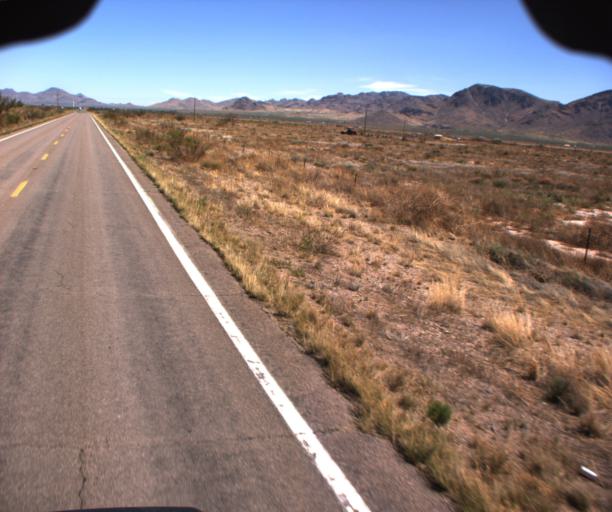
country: US
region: New Mexico
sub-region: Hidalgo County
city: Lordsburg
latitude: 31.8080
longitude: -109.0511
